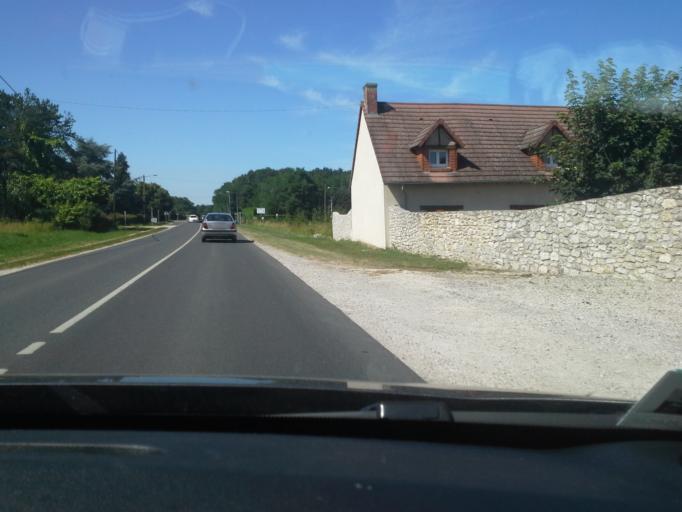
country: FR
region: Centre
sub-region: Departement du Loir-et-Cher
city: Cormeray
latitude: 47.4948
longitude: 1.4056
